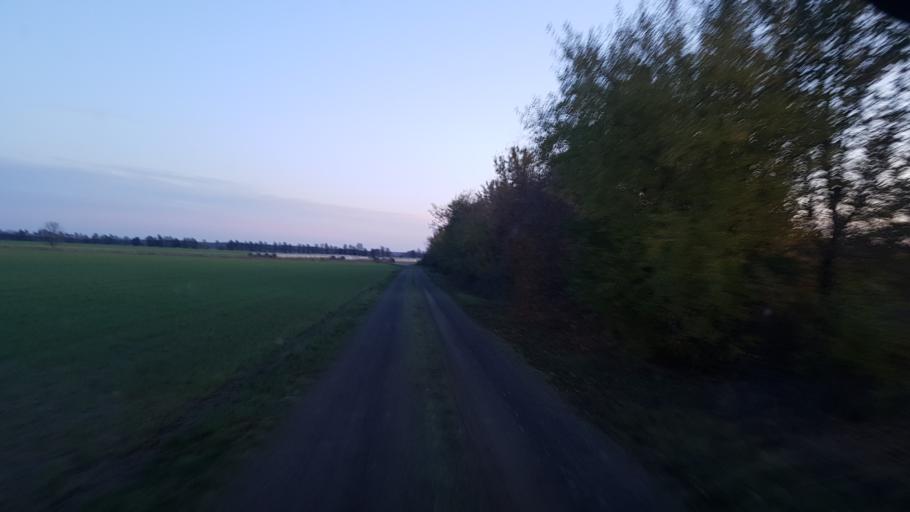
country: DE
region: Brandenburg
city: Schilda
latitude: 51.6294
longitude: 13.3289
